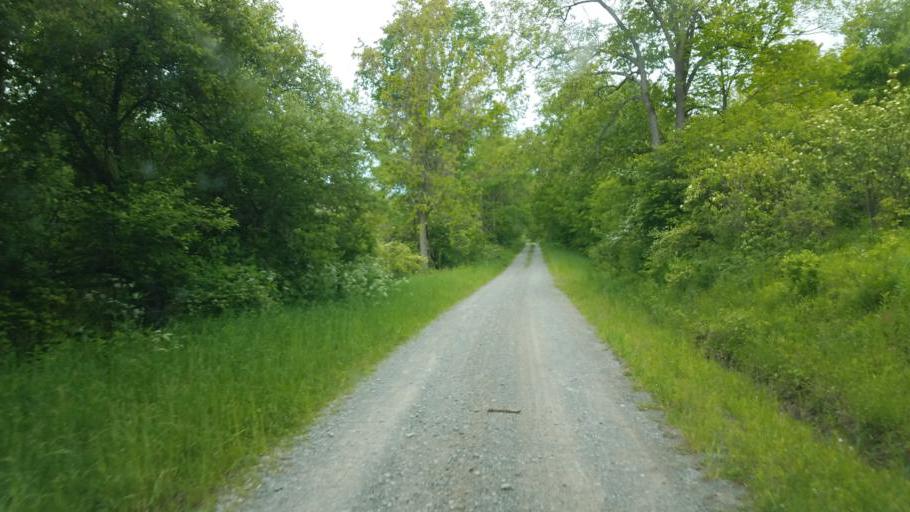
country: US
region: New York
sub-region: Herkimer County
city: Ilion
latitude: 42.9036
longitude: -75.1145
